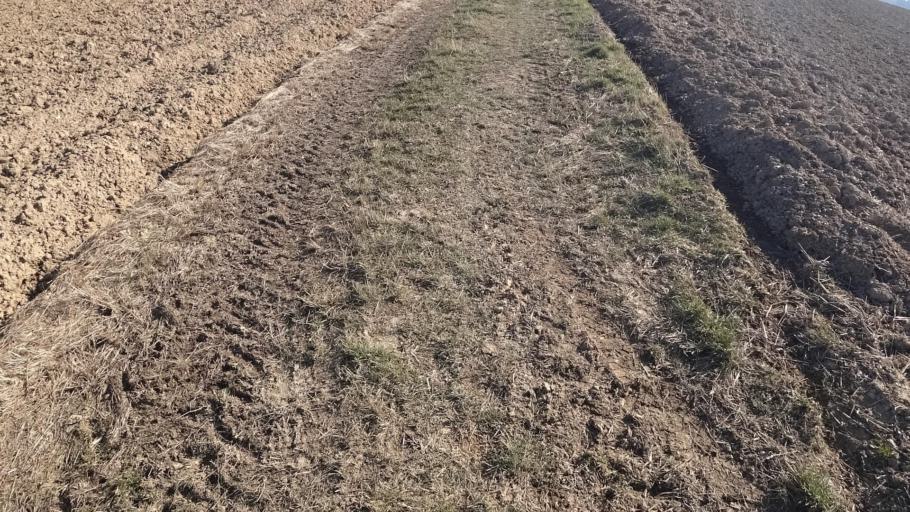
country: DE
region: Rheinland-Pfalz
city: Mutterschied
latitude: 49.9890
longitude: 7.5630
